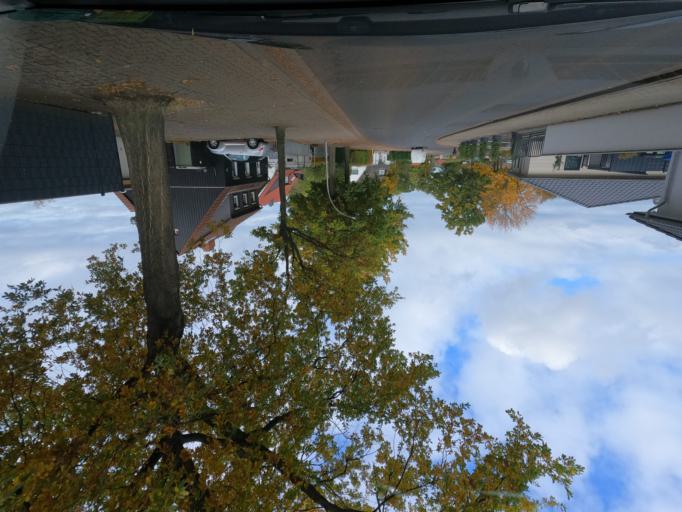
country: DE
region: Lower Saxony
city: Leiferde
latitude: 52.1941
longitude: 10.4775
